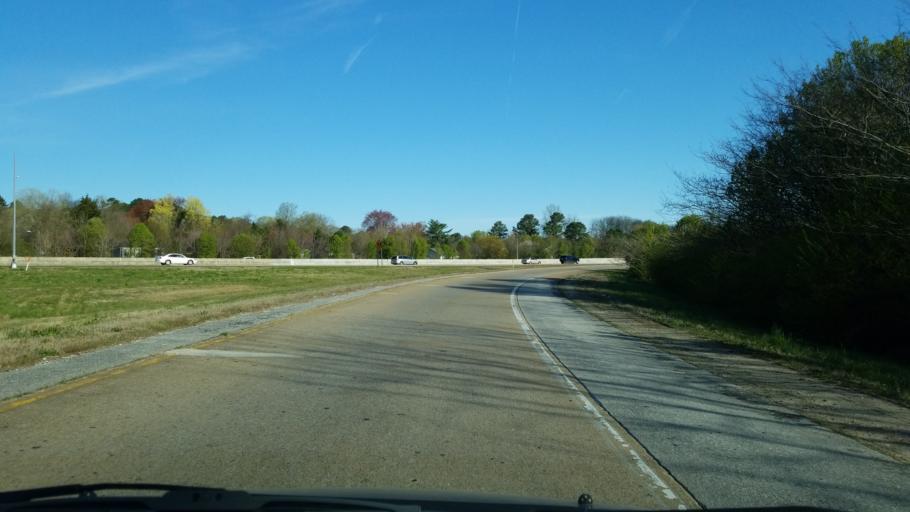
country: US
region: Tennessee
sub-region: Hamilton County
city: East Brainerd
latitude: 35.0186
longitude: -85.1765
